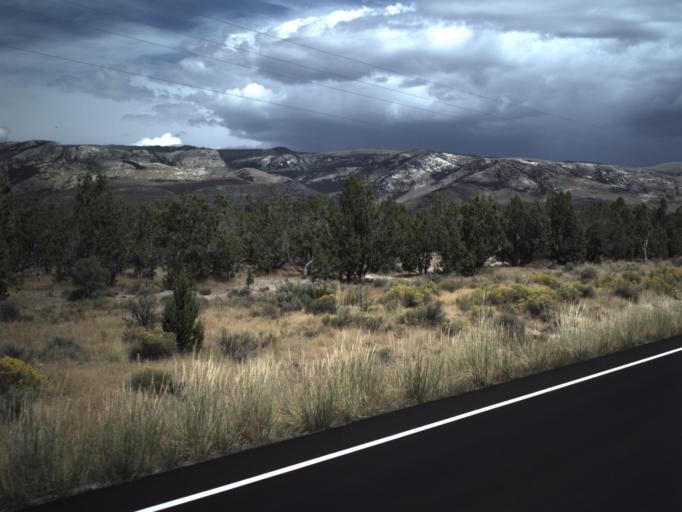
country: US
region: Idaho
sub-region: Cassia County
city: Burley
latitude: 41.8142
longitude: -113.4375
